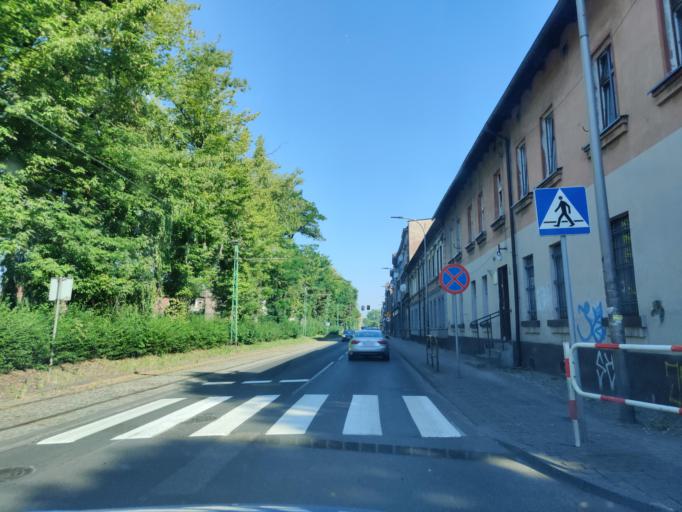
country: PL
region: Silesian Voivodeship
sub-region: Sosnowiec
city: Sosnowiec
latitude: 50.2486
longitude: 19.1327
